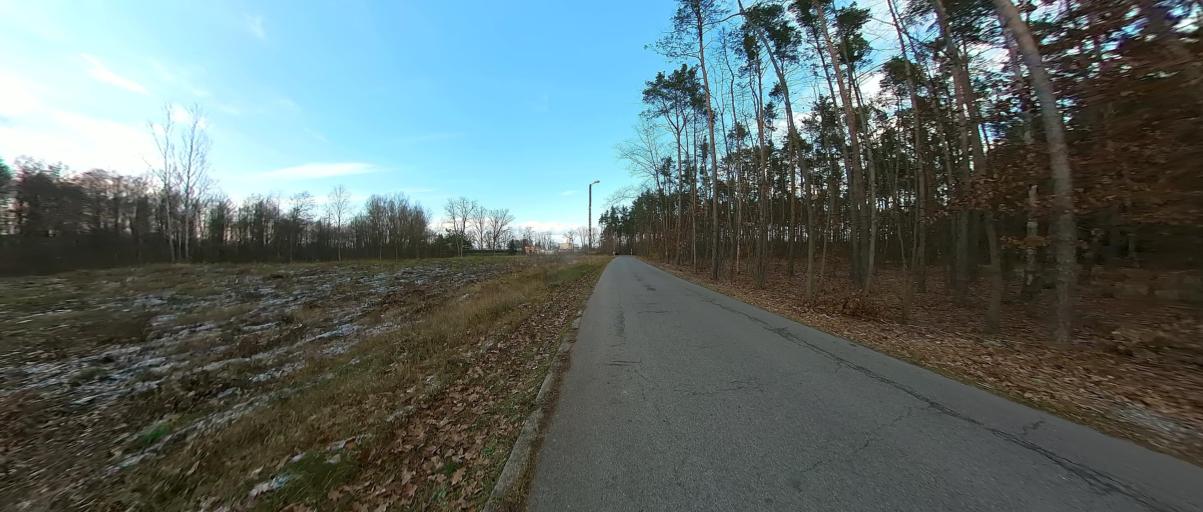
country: PL
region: Masovian Voivodeship
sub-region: Powiat bialobrzeski
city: Bialobrzegi
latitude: 51.6490
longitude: 20.9646
